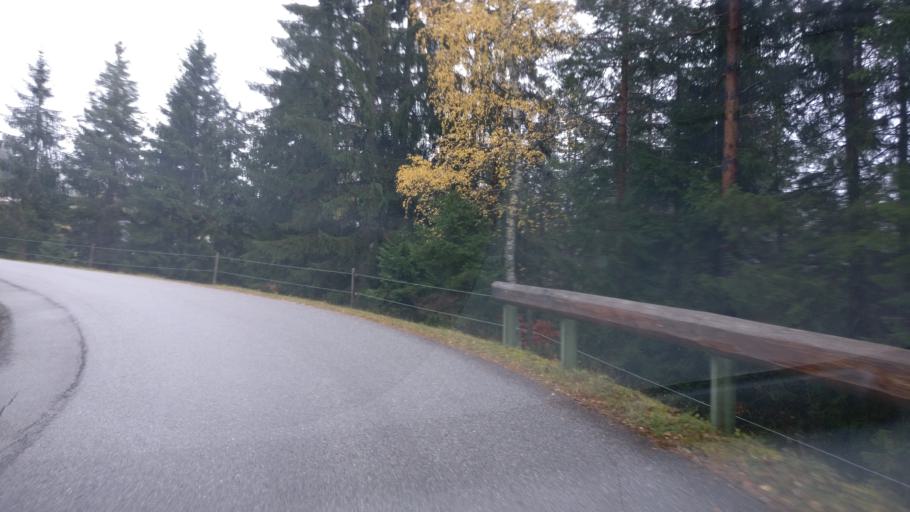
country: AT
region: Salzburg
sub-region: Politischer Bezirk Sankt Johann im Pongau
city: Filzmoos
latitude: 47.3994
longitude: 13.5198
